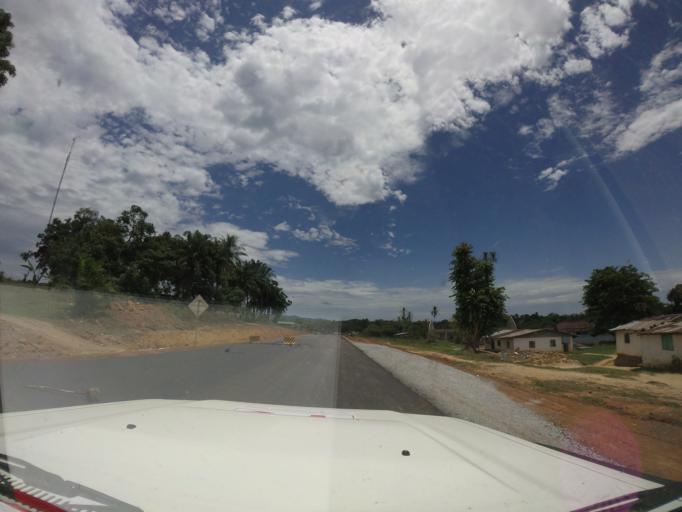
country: LR
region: Margibi
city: Kakata
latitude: 6.7475
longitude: -10.1112
